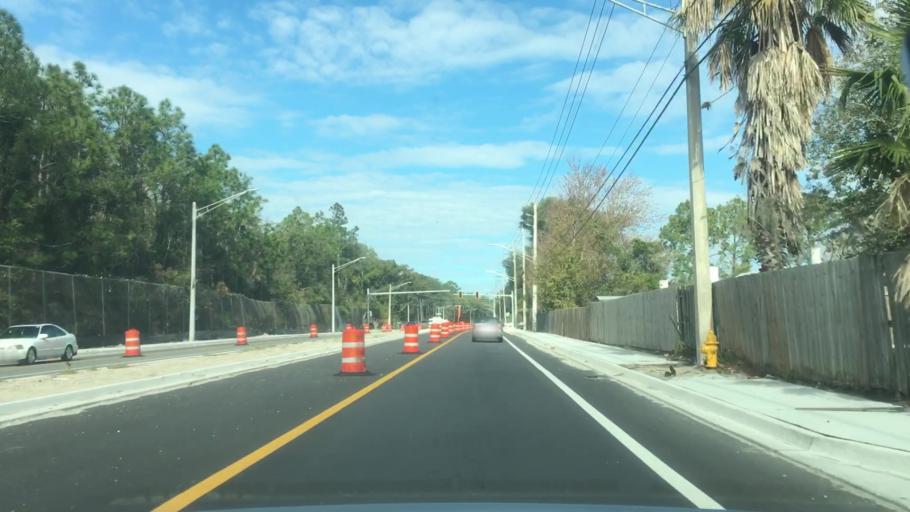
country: US
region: Florida
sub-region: Duval County
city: Atlantic Beach
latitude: 30.3235
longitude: -81.4723
